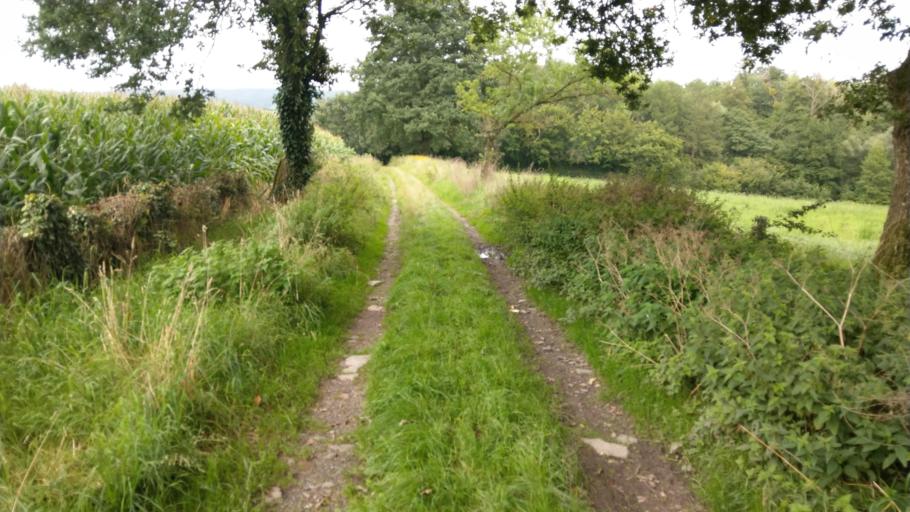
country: BE
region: Wallonia
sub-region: Province de Liege
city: Plombieres
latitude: 50.7374
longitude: 5.9332
